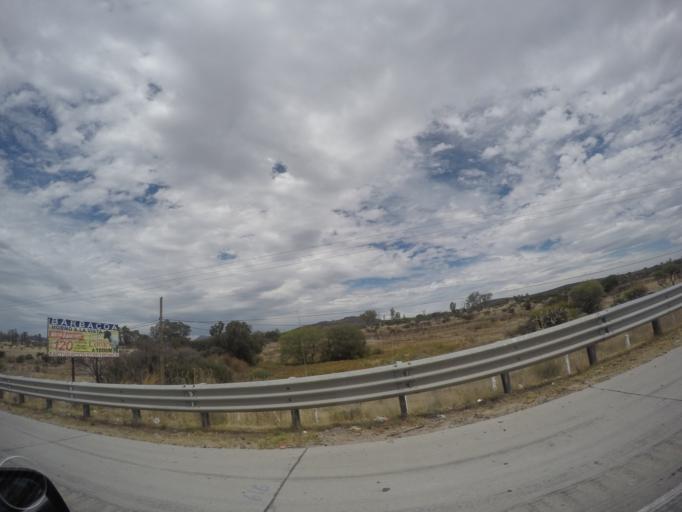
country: MX
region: Queretaro
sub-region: San Juan del Rio
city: Paso de Mata
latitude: 20.3153
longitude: -99.9309
